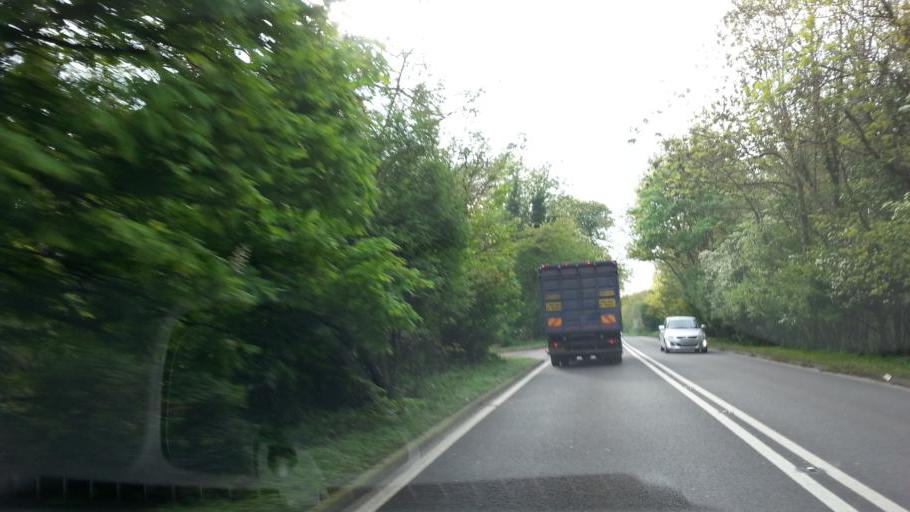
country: GB
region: England
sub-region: Nottinghamshire
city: South Collingham
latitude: 53.0799
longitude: -0.7138
